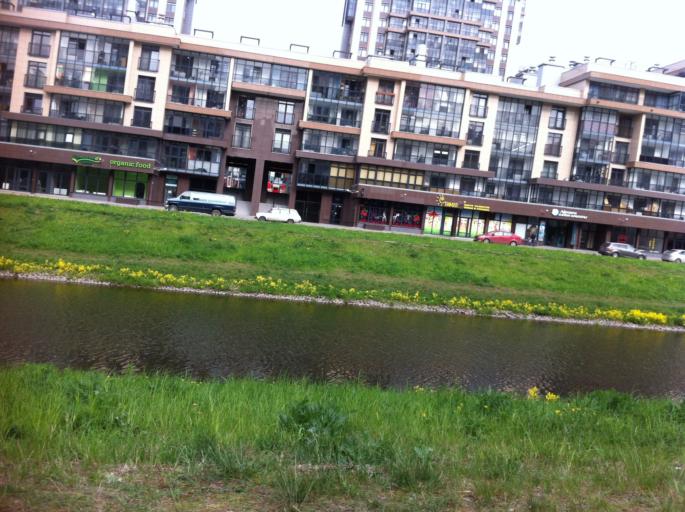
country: RU
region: St.-Petersburg
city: Sosnovaya Polyana
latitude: 59.8527
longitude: 30.1442
